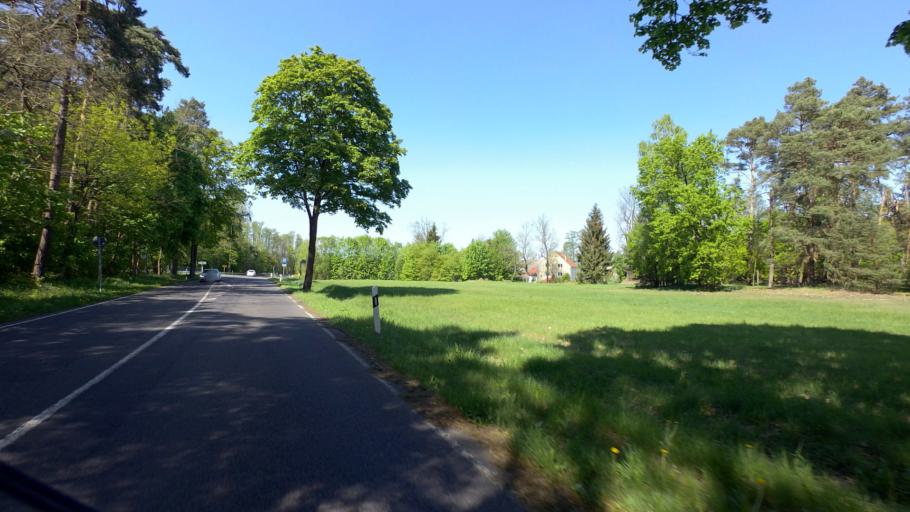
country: DE
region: Brandenburg
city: Friedland
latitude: 52.0860
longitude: 14.2601
